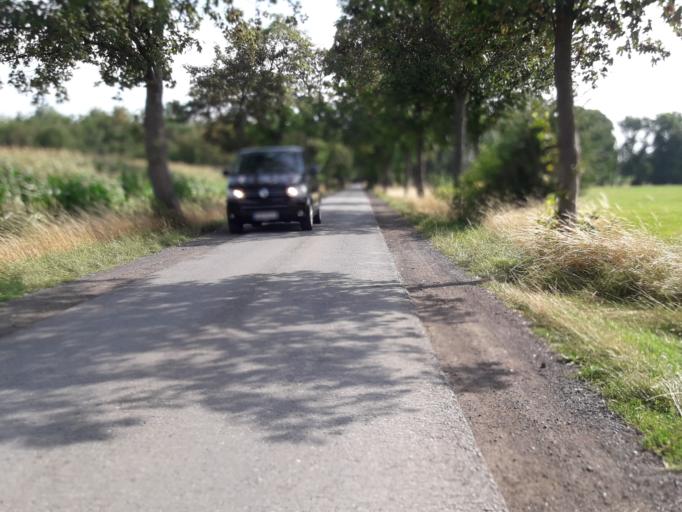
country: DE
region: North Rhine-Westphalia
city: Bad Lippspringe
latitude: 51.7484
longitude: 8.7945
